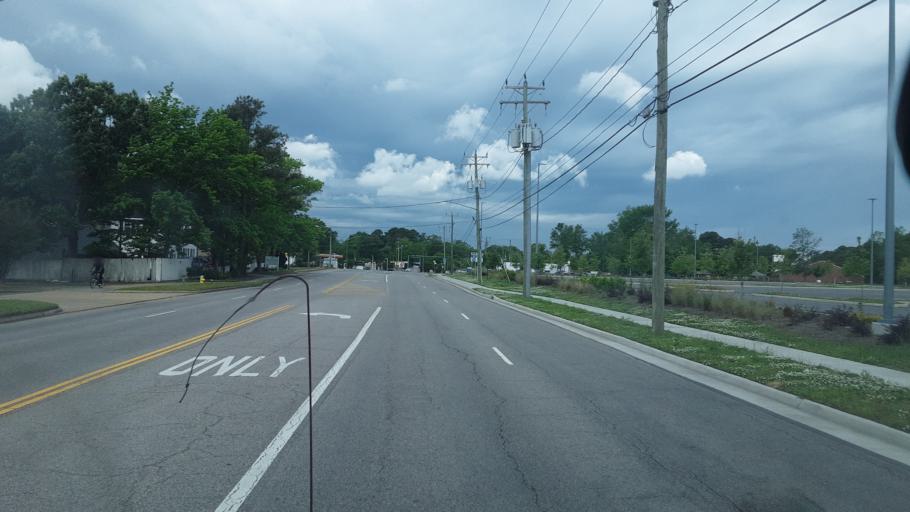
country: US
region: Virginia
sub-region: City of Virginia Beach
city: Virginia Beach
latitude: 36.8422
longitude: -75.9928
